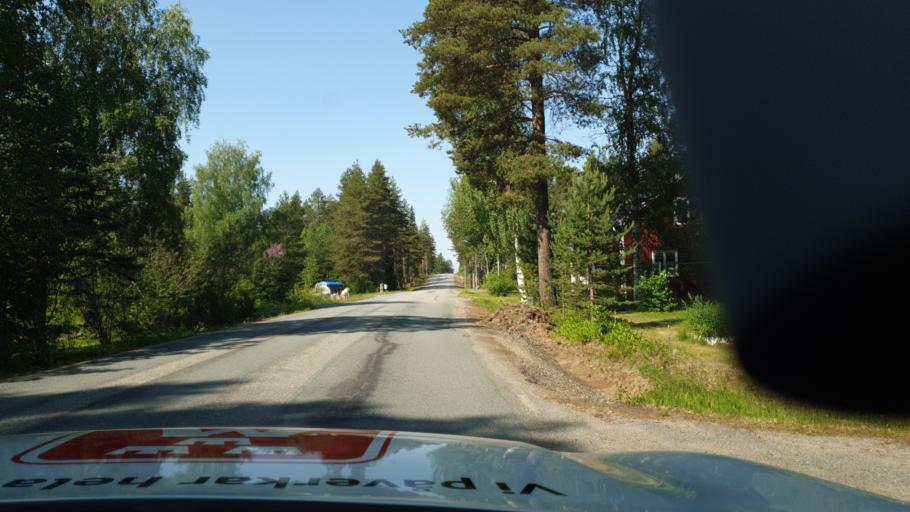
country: SE
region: Vaesterbotten
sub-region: Skelleftea Kommun
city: Langsele
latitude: 64.9399
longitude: 19.9902
